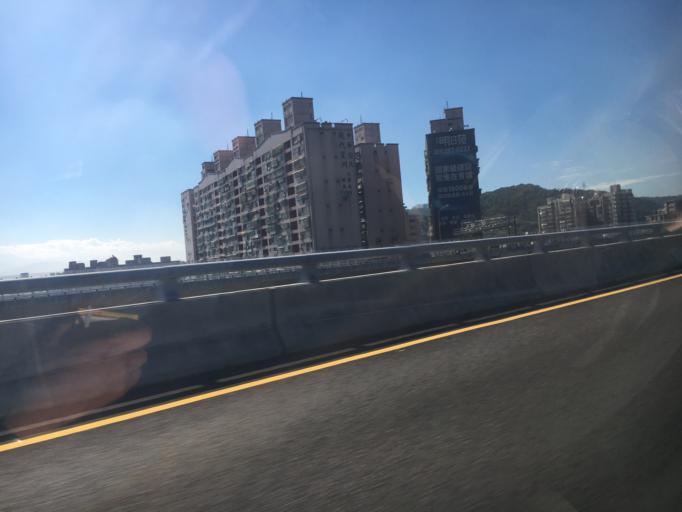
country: TW
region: Taipei
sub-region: Taipei
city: Banqiao
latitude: 25.0689
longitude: 121.4361
